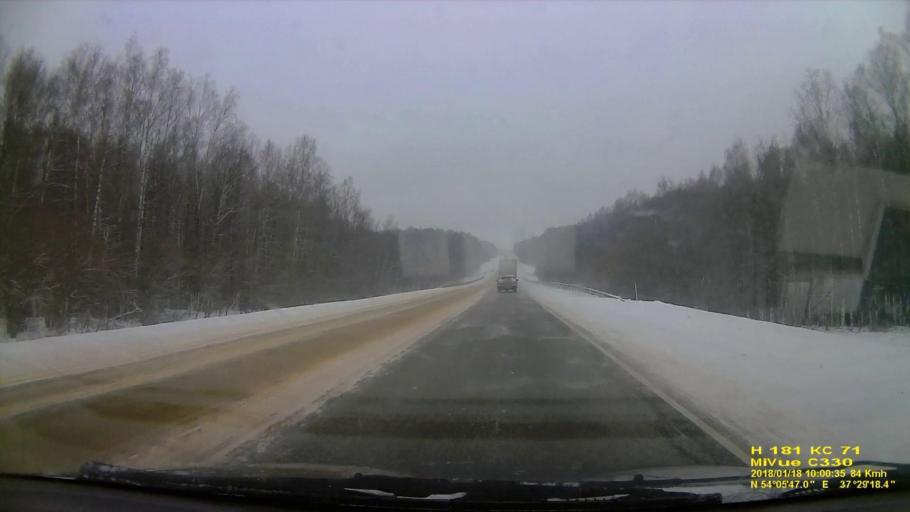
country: RU
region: Tula
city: Pervomayskiy
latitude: 54.0963
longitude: 37.4885
